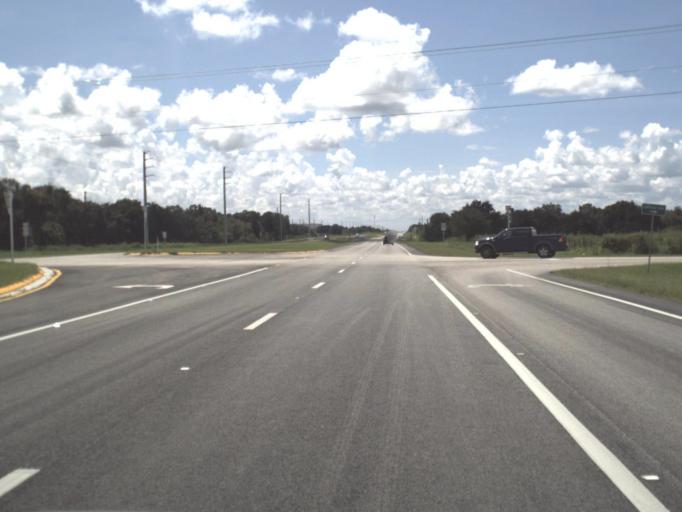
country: US
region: Florida
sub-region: Charlotte County
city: Harbour Heights
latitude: 27.0684
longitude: -81.9584
